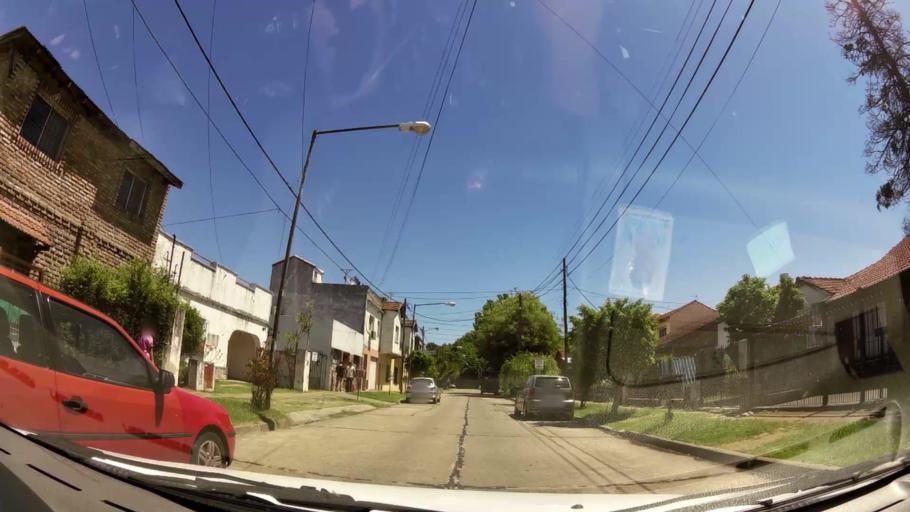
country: AR
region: Buenos Aires
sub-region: Partido de San Isidro
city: San Isidro
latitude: -34.5012
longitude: -58.5323
